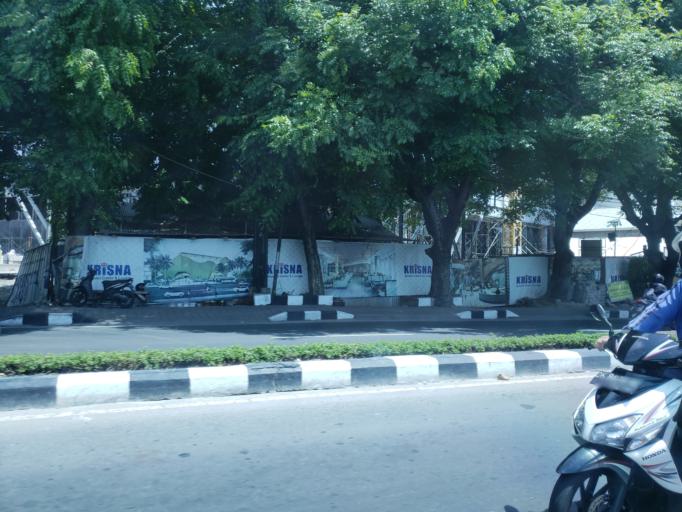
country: ID
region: Bali
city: Jabajero
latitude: -8.7295
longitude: 115.1792
